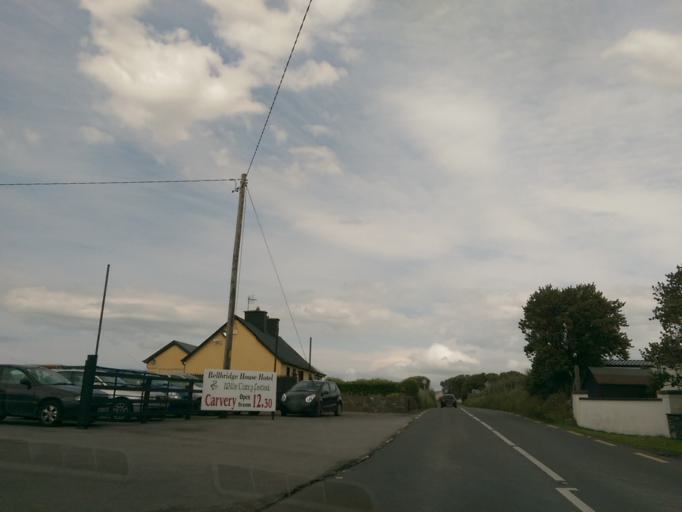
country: IE
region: Munster
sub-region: An Clar
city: Kilrush
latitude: 52.8377
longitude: -9.4291
